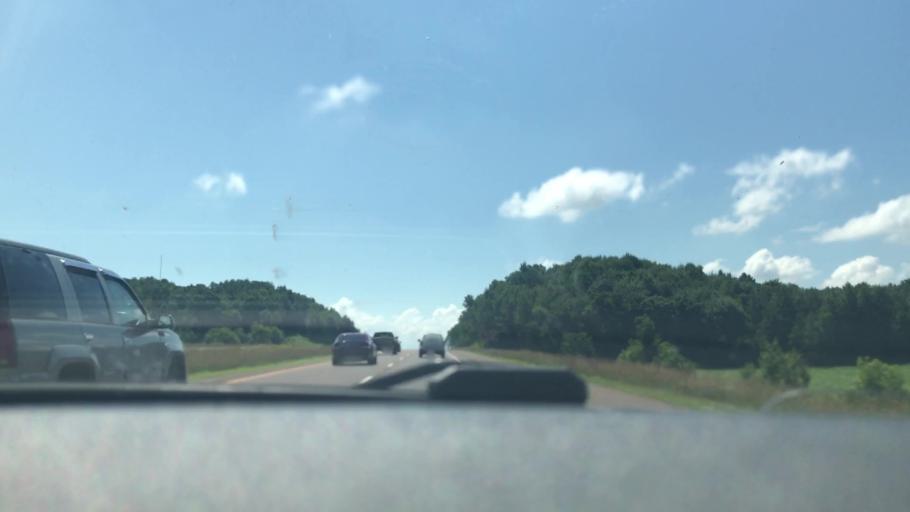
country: US
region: Wisconsin
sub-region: Chippewa County
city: Chippewa Falls
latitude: 44.9792
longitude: -91.4378
